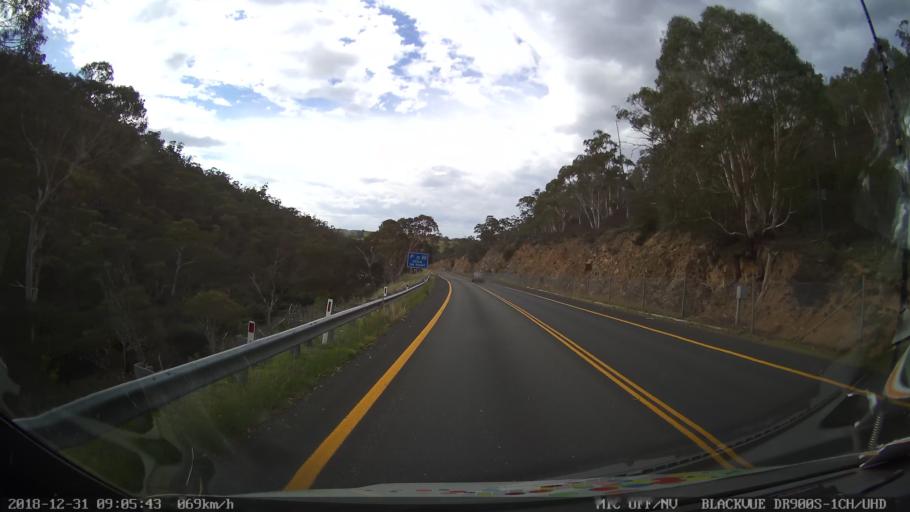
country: AU
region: New South Wales
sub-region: Snowy River
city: Jindabyne
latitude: -36.3661
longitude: 148.5877
